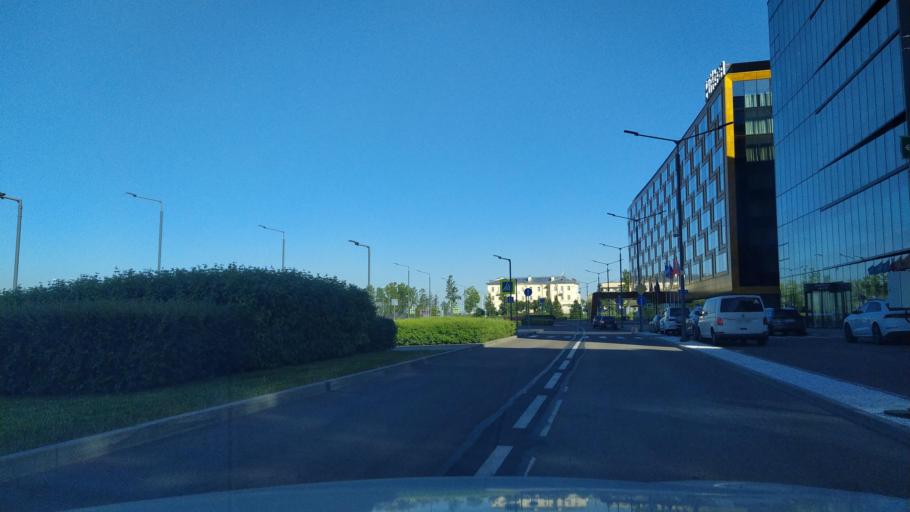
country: RU
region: St.-Petersburg
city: Aleksandrovskaya
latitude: 59.7636
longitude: 30.3567
